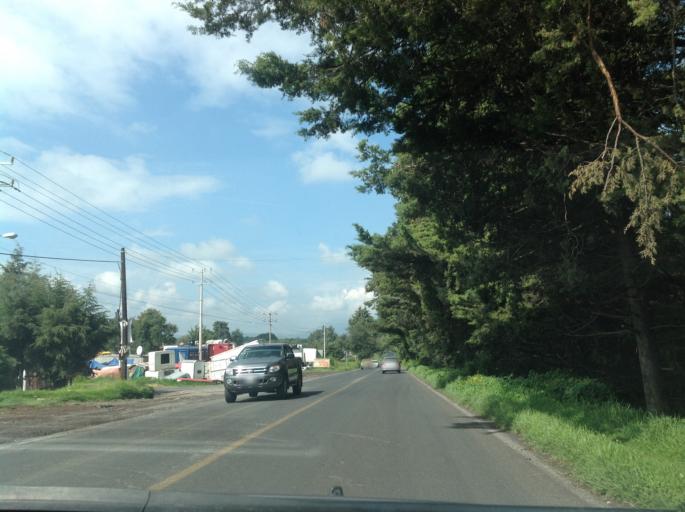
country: MX
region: Mexico
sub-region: Xalatlaco
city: Mezapa la Fabrica
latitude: 19.1785
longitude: -99.4441
